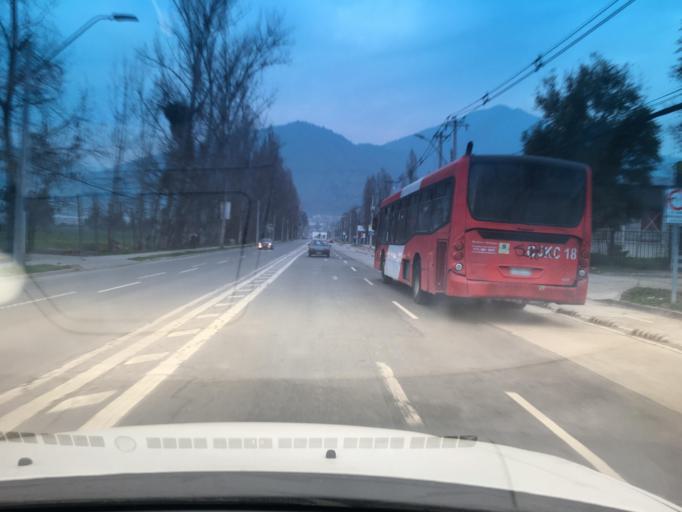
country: CL
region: Santiago Metropolitan
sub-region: Provincia de Santiago
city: Santiago
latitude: -33.3915
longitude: -70.6239
